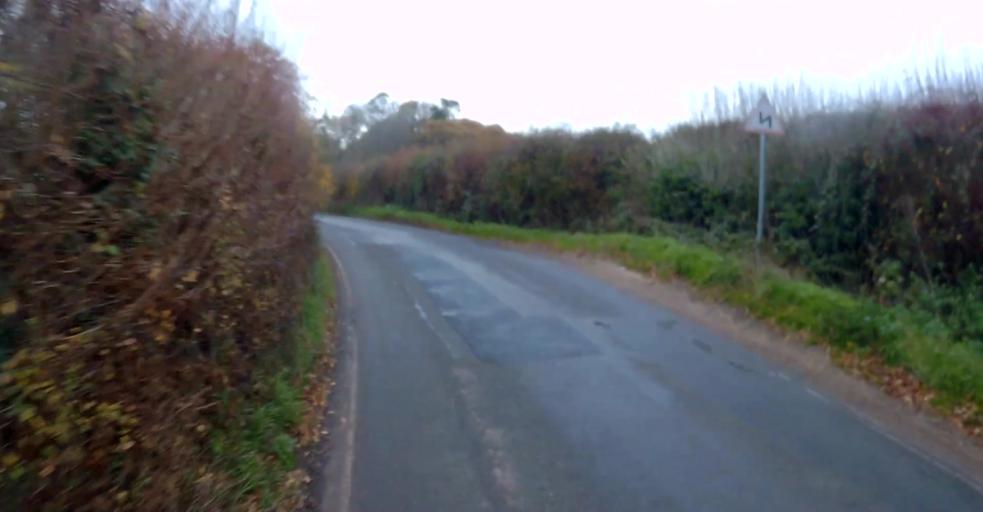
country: GB
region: England
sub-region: Wokingham
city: Swallowfield
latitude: 51.3809
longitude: -0.9346
